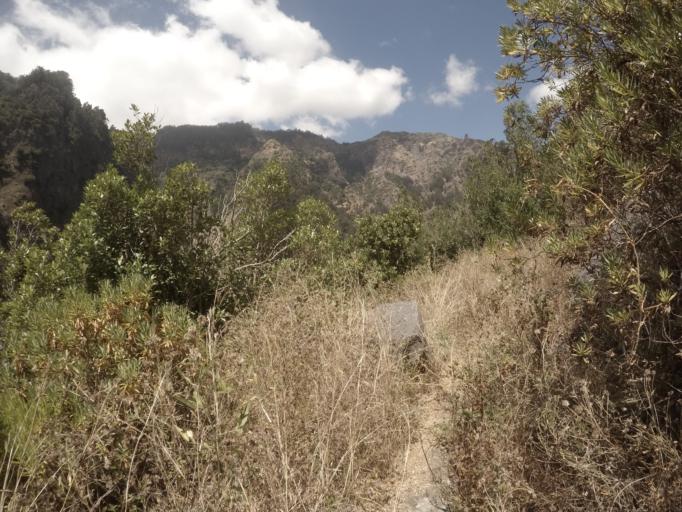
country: PT
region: Madeira
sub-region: Camara de Lobos
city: Curral das Freiras
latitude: 32.7032
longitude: -16.9663
